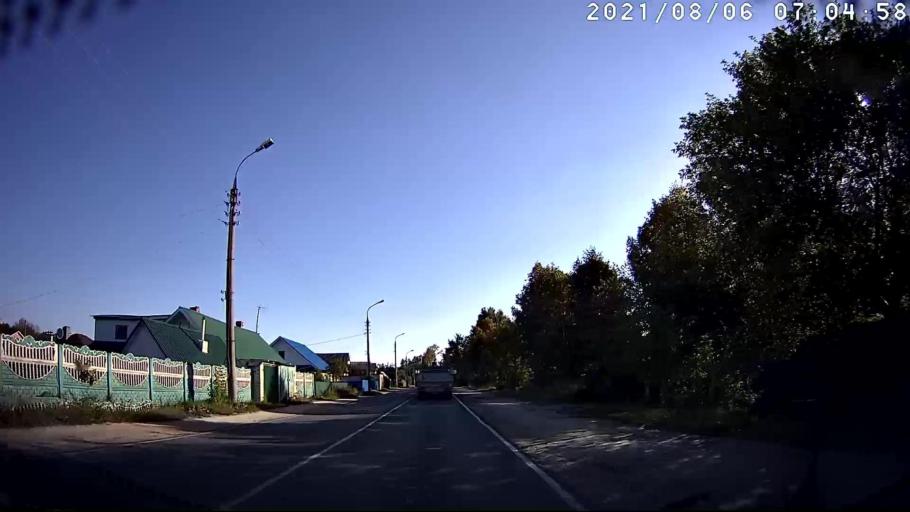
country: RU
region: Mariy-El
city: Yoshkar-Ola
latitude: 56.5506
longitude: 47.9845
